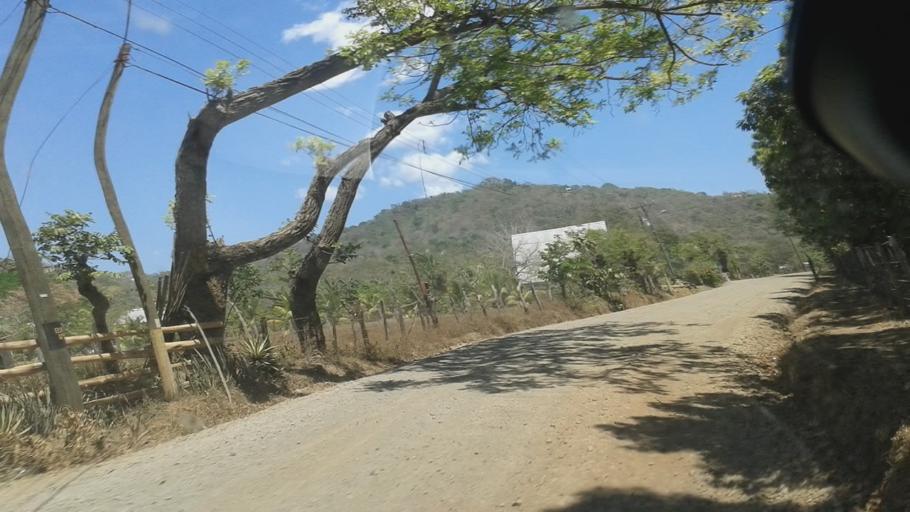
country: CR
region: Guanacaste
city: Samara
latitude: 9.9937
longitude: -85.6756
